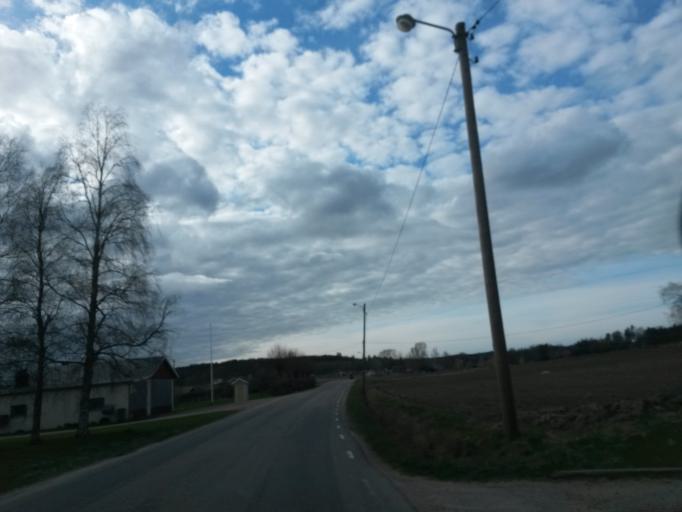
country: SE
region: Vaestra Goetaland
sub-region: Vargarda Kommun
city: Jonstorp
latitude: 58.0174
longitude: 12.6448
